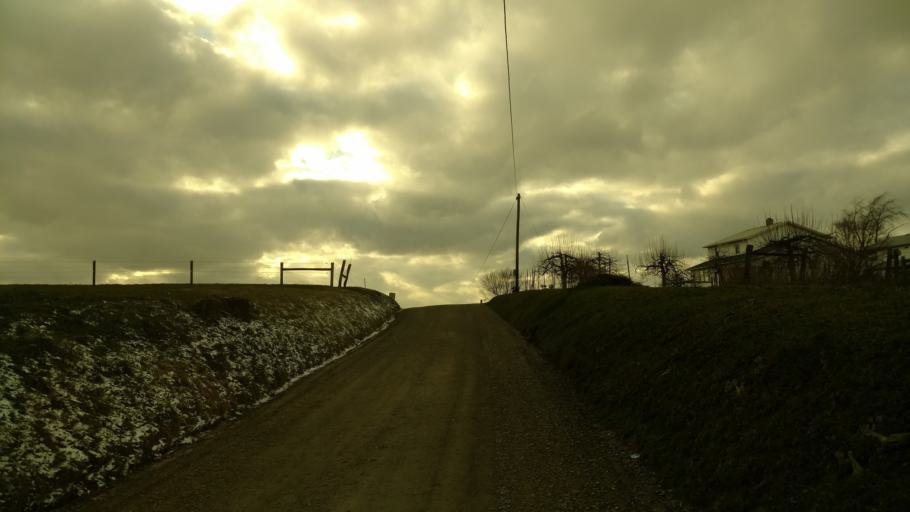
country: US
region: Ohio
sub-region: Tuscarawas County
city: Sugarcreek
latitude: 40.5053
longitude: -81.7380
